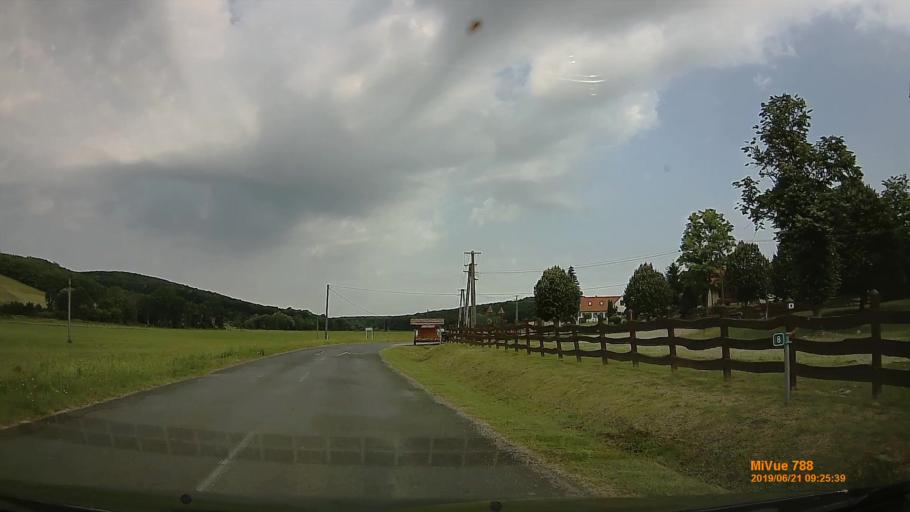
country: HU
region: Somogy
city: Taszar
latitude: 46.2672
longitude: 17.9072
